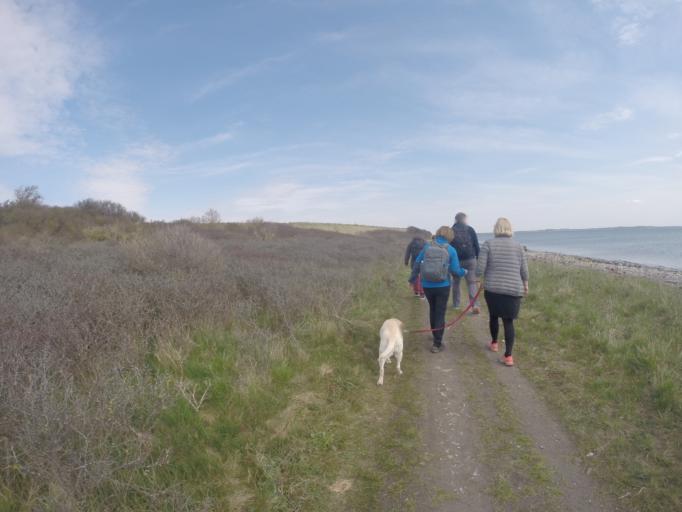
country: DK
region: Zealand
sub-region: Kalundborg Kommune
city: Gorlev
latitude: 55.5108
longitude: 11.0999
